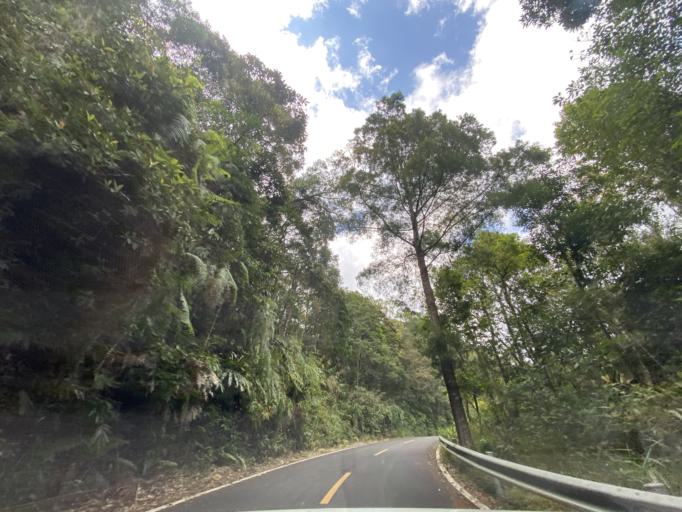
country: CN
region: Hainan
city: Benhao
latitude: 18.6966
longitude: 109.8795
